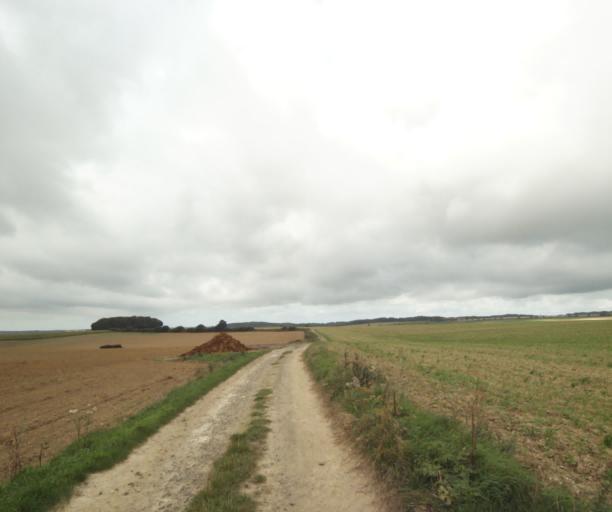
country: FR
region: Nord-Pas-de-Calais
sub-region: Departement du Pas-de-Calais
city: Etaples
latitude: 50.5310
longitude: 1.6773
